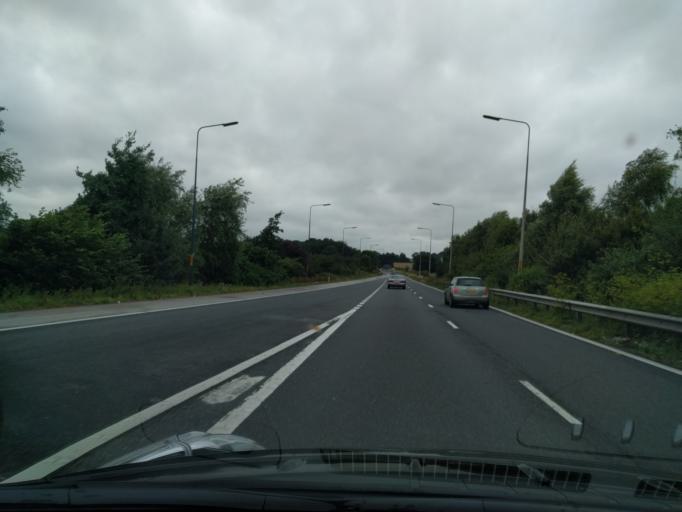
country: GB
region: England
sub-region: Warrington
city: Croft
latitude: 53.4296
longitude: -2.5653
